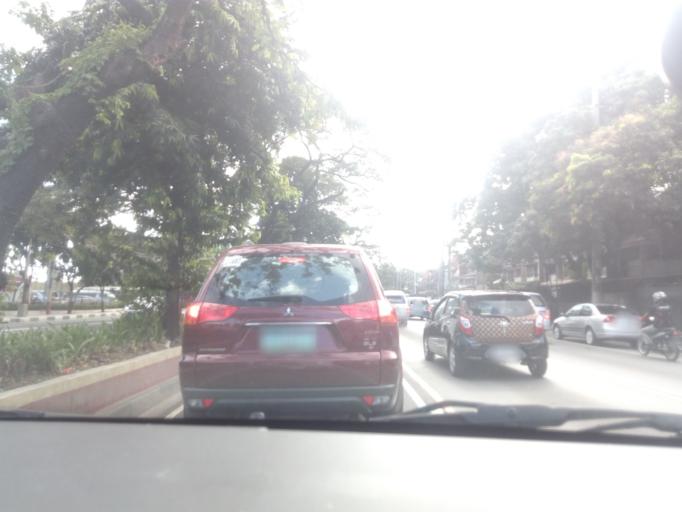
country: PH
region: Metro Manila
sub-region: Pasig
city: Pasig City
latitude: 14.5800
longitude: 121.0750
